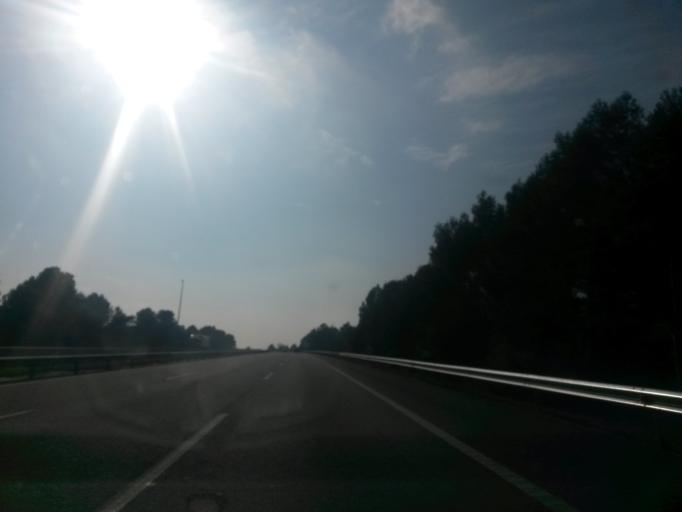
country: ES
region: Catalonia
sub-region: Provincia de Girona
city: Garrigas
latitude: 42.2011
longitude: 2.9350
